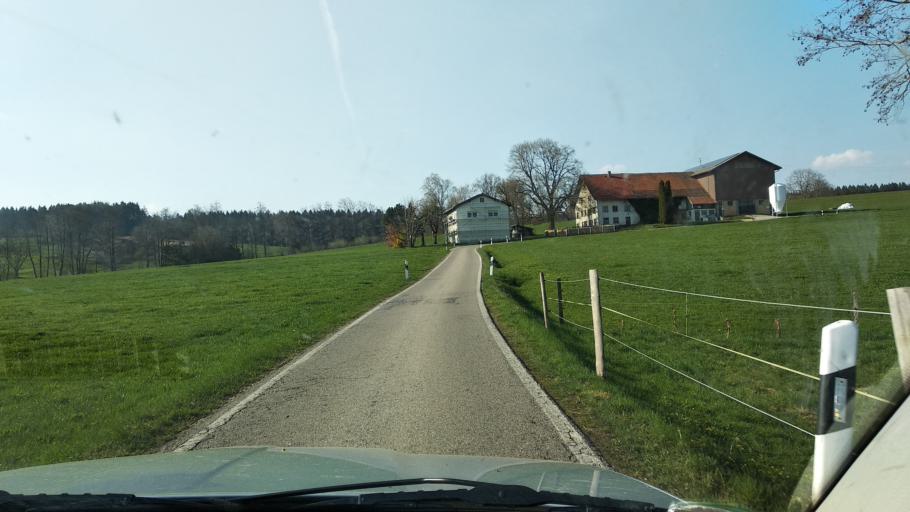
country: DE
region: Baden-Wuerttemberg
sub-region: Tuebingen Region
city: Leutkirch im Allgau
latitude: 47.8390
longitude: 10.0671
